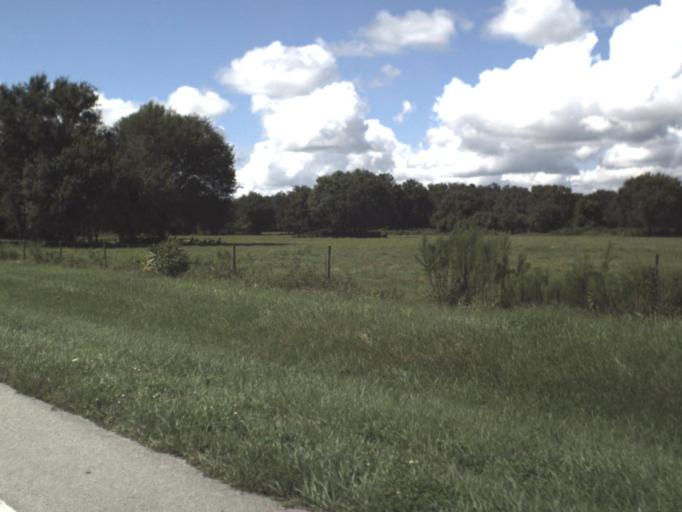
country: US
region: Florida
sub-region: DeSoto County
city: Arcadia
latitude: 27.2311
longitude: -81.9017
